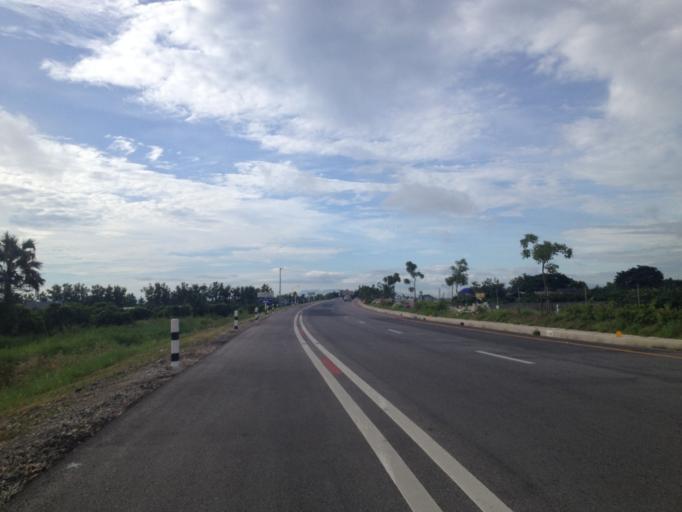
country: TH
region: Chiang Mai
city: San Pa Tong
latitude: 18.5657
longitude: 98.8499
